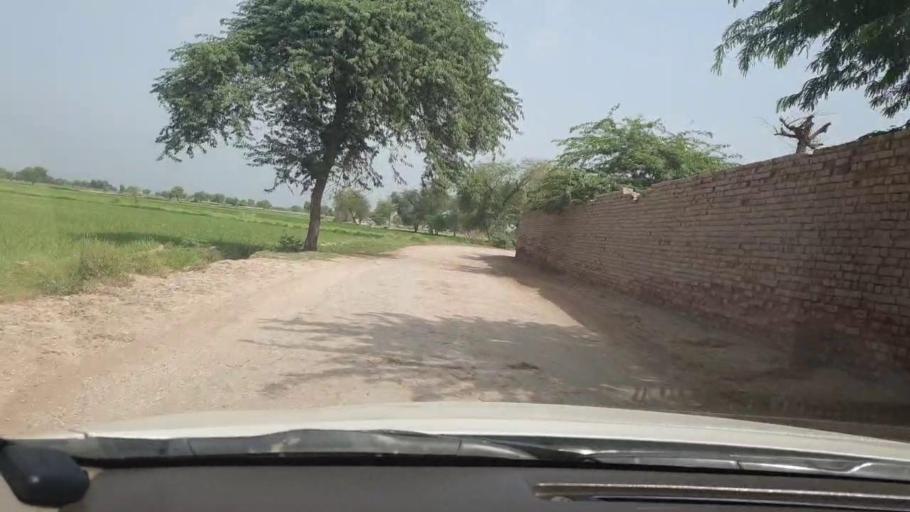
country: PK
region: Sindh
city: Shikarpur
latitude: 27.9994
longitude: 68.5953
